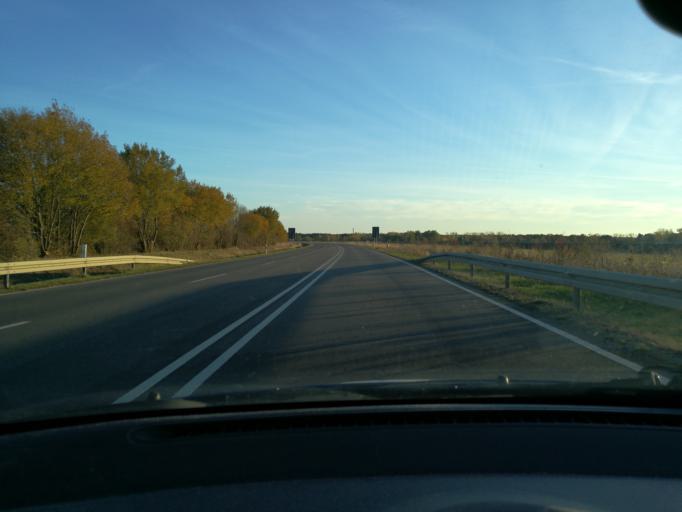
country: DE
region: Brandenburg
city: Perleberg
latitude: 53.0747
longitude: 11.8281
